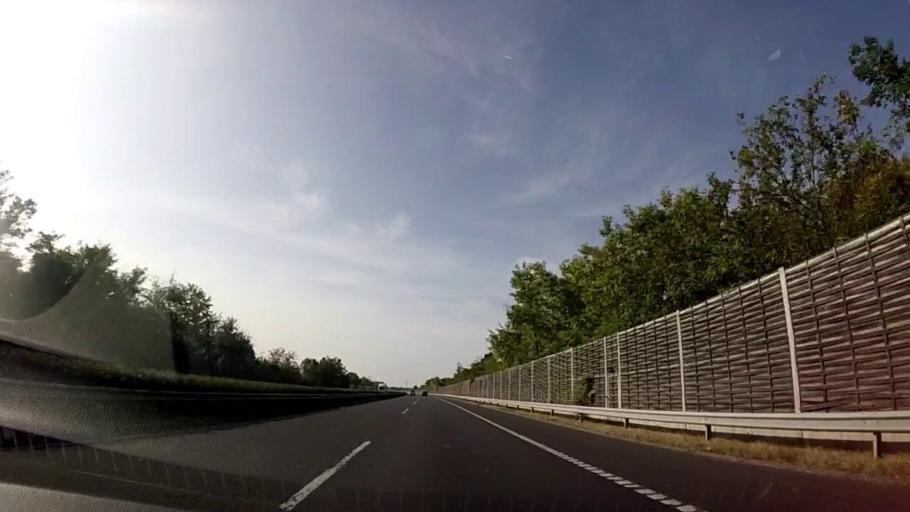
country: HU
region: Fejer
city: Lepseny
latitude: 46.9857
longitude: 18.1802
